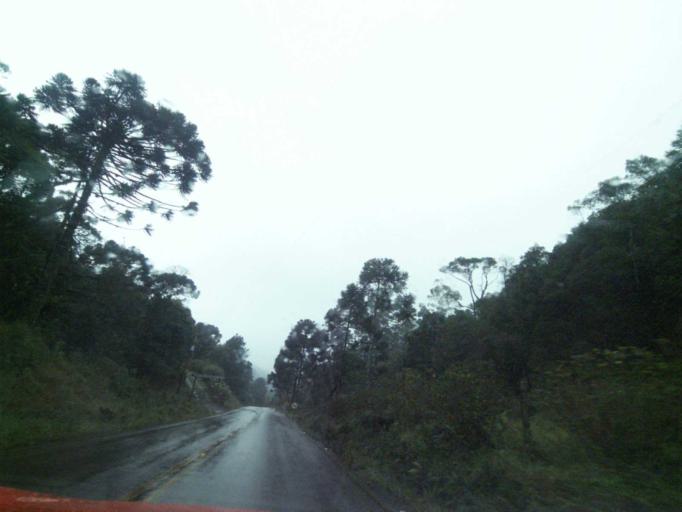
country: BR
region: Santa Catarina
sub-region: Anitapolis
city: Anitapolis
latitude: -27.8014
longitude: -49.0459
